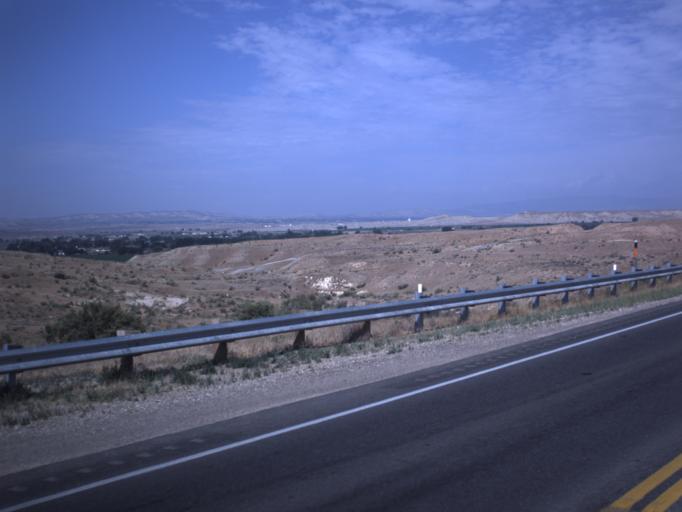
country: US
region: Utah
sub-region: Uintah County
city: Naples
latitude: 40.3637
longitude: -109.3207
